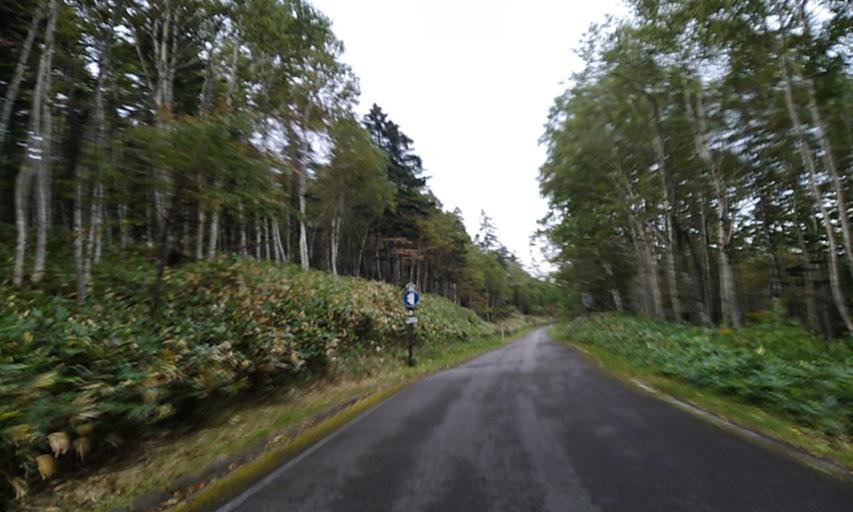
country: JP
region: Hokkaido
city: Bihoro
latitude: 43.5739
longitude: 144.2267
